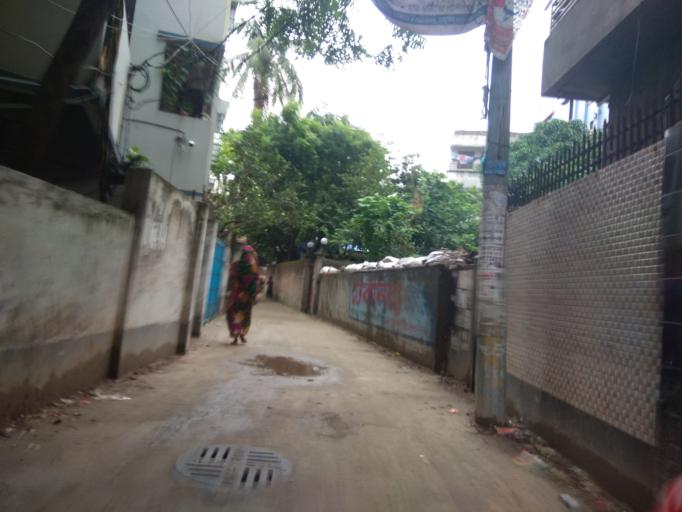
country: BD
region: Dhaka
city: Azimpur
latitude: 23.7948
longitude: 90.3675
